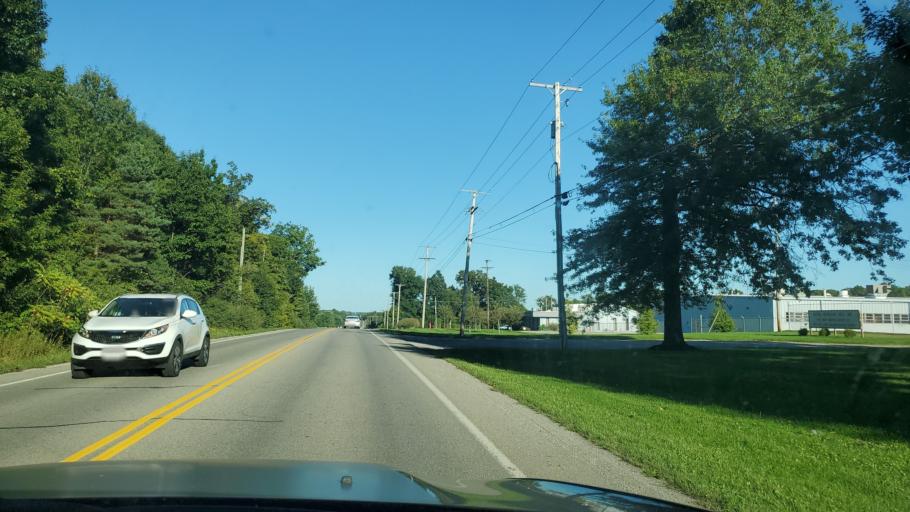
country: US
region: Ohio
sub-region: Mahoning County
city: Canfield
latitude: 40.9882
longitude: -80.7484
